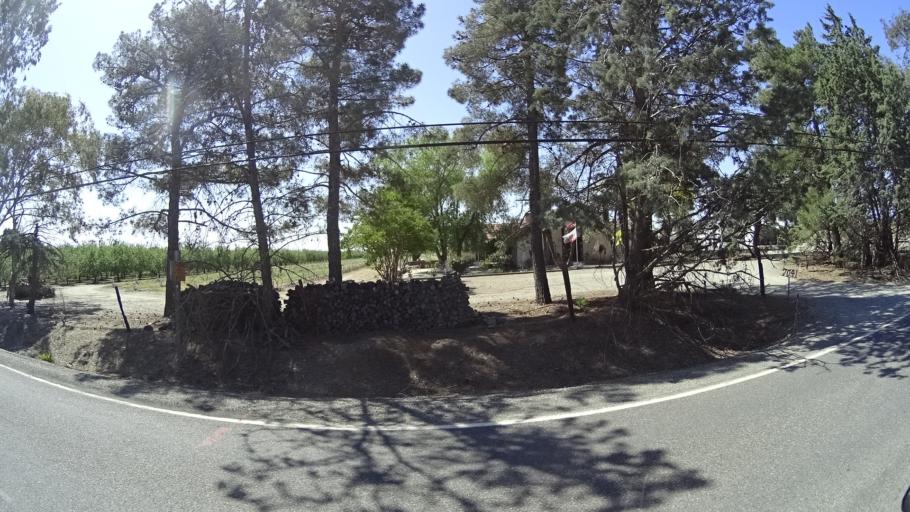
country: US
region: California
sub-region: Glenn County
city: Orland
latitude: 39.7106
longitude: -122.1363
